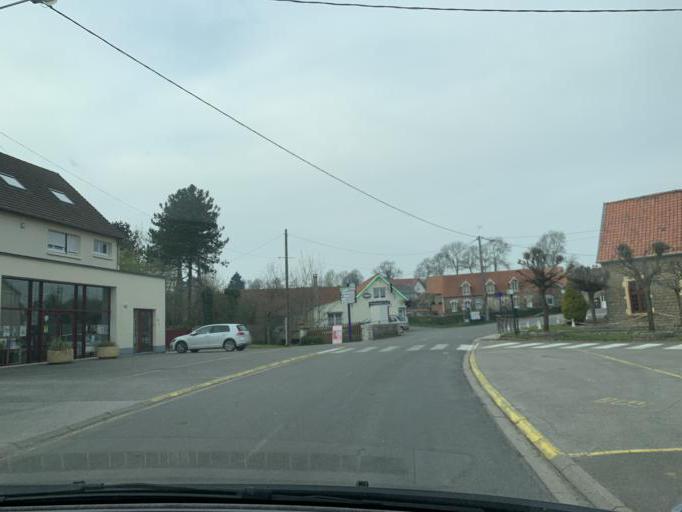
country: FR
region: Nord-Pas-de-Calais
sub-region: Departement du Pas-de-Calais
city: Samer
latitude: 50.6843
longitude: 1.7607
